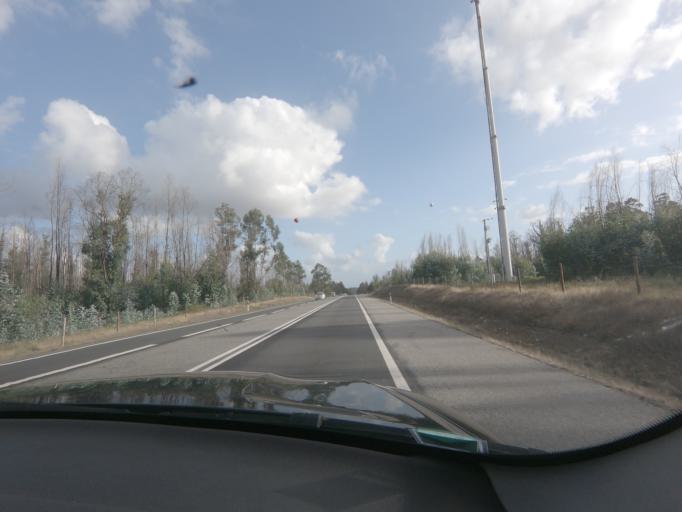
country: PT
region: Viseu
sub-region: Concelho de Tondela
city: Tondela
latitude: 40.5611
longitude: -8.0511
